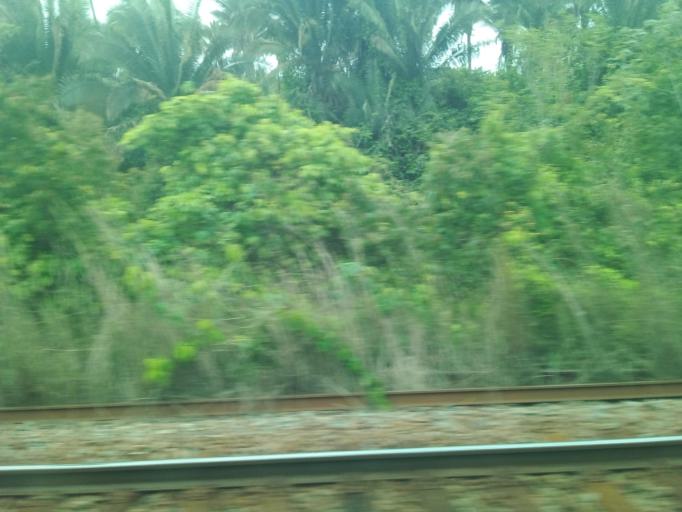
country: BR
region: Maranhao
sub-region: Santa Ines
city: Santa Ines
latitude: -3.6524
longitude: -45.7996
